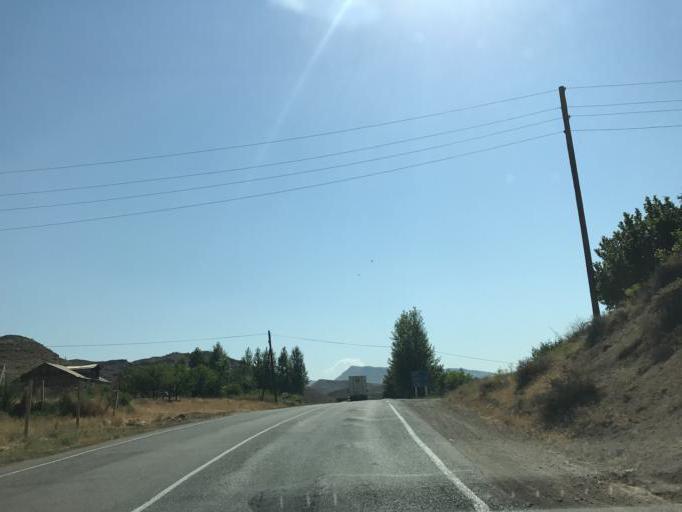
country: AM
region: Vayots' Dzori Marz
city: Yeghegnadzor
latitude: 39.7574
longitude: 45.3452
